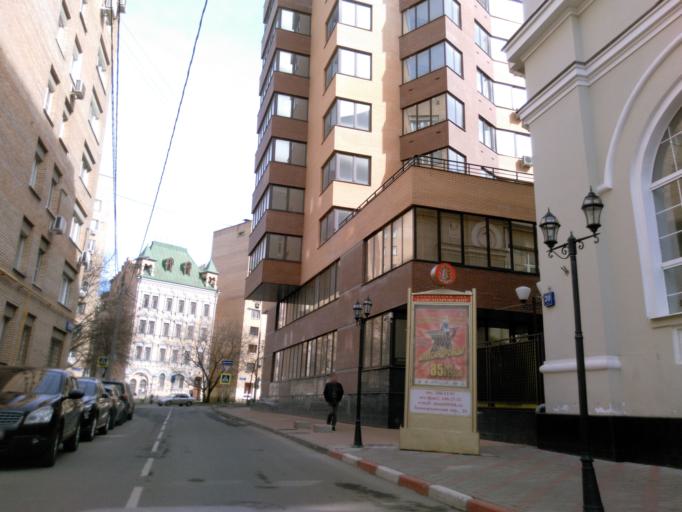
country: RU
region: Moskovskaya
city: Dorogomilovo
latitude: 55.7424
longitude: 37.5791
